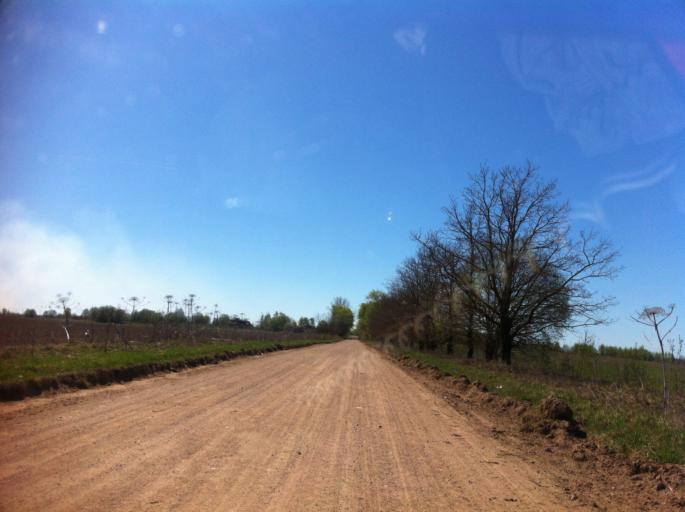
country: RU
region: Pskov
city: Izborsk
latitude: 57.7948
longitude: 27.9637
